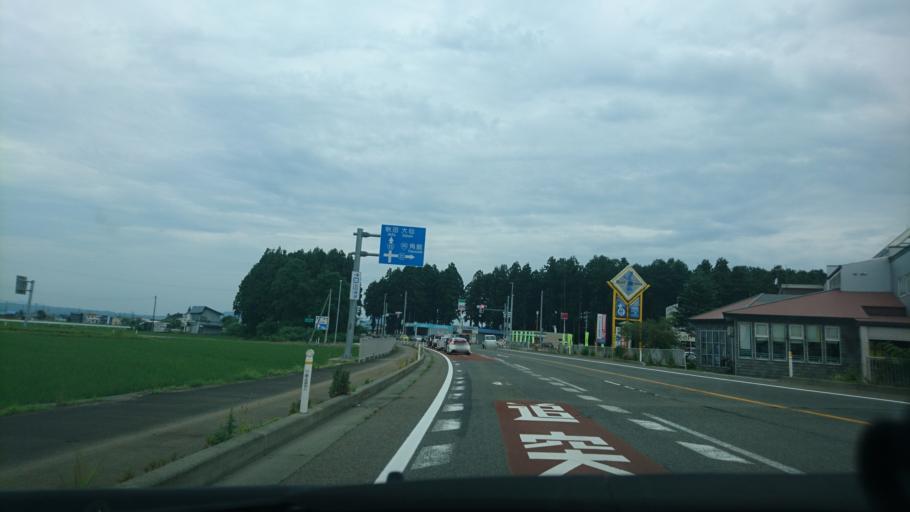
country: JP
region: Akita
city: Omagari
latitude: 39.4146
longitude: 140.5516
